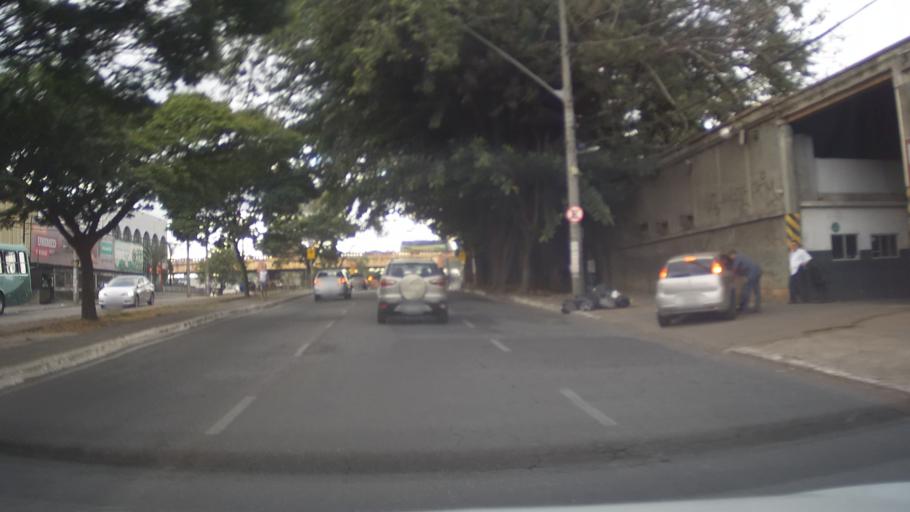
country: BR
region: Minas Gerais
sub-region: Contagem
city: Contagem
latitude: -19.9538
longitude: -44.0179
